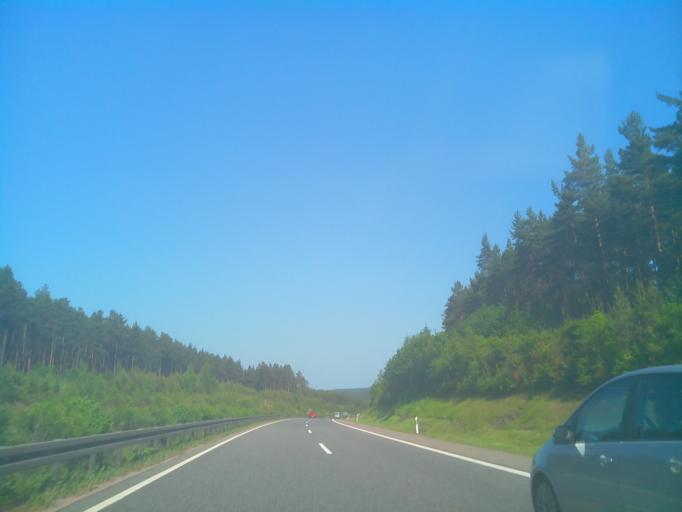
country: DE
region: Thuringia
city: Ilmenau
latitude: 50.7145
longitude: 10.9185
